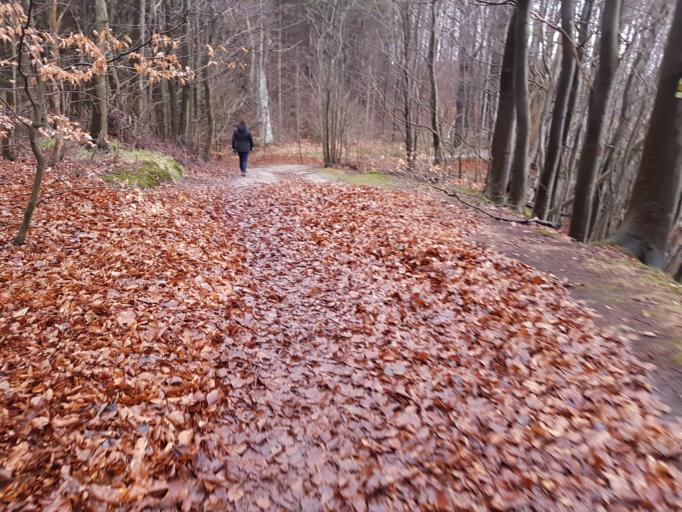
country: DE
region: Mecklenburg-Vorpommern
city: Ostseebad Sellin
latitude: 54.3990
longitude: 13.6737
